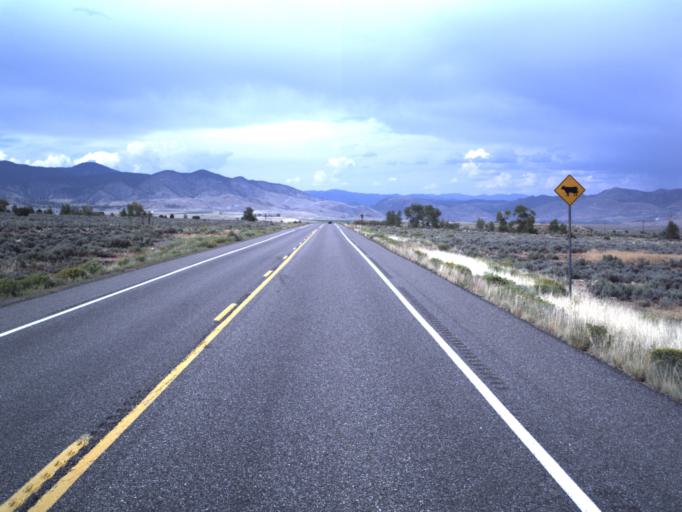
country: US
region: Utah
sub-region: Piute County
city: Junction
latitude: 38.3802
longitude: -112.2280
